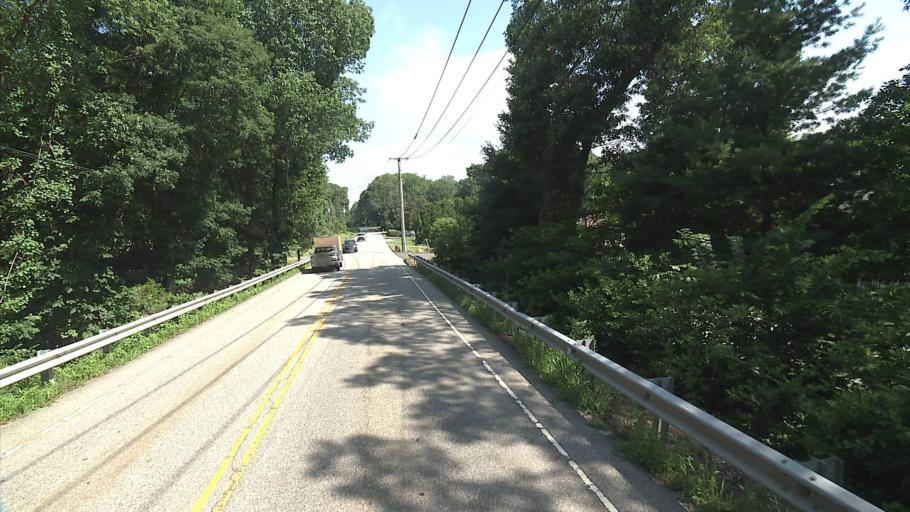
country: US
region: Connecticut
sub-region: Middlesex County
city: Clinton
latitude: 41.2779
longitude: -72.4854
